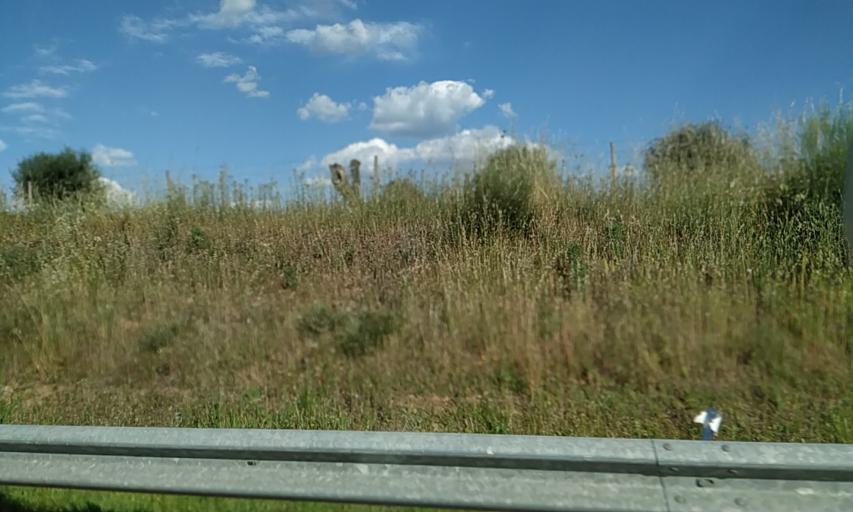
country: PT
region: Evora
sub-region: Estremoz
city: Estremoz
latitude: 38.9611
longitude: -7.5090
